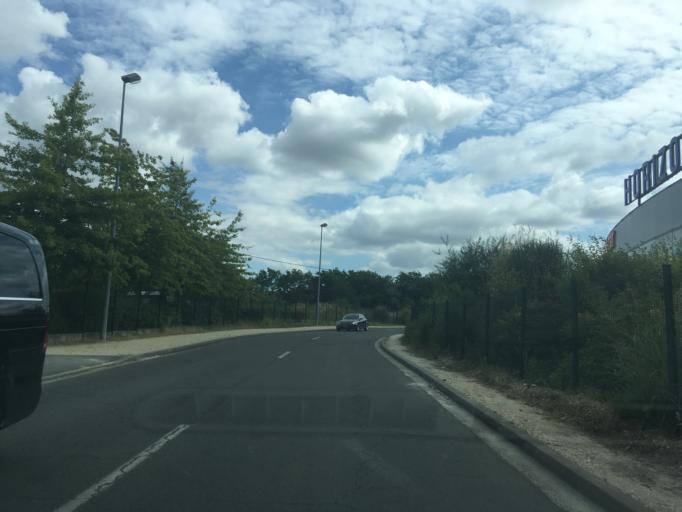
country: FR
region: Aquitaine
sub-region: Departement de la Gironde
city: Eysines
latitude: 44.8654
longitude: -0.6549
